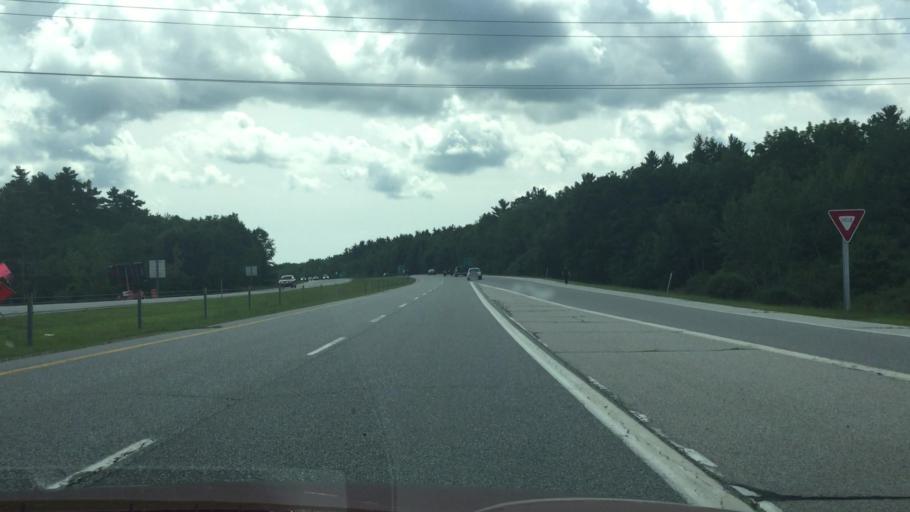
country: US
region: Maine
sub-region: York County
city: Saco
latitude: 43.5198
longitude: -70.4429
